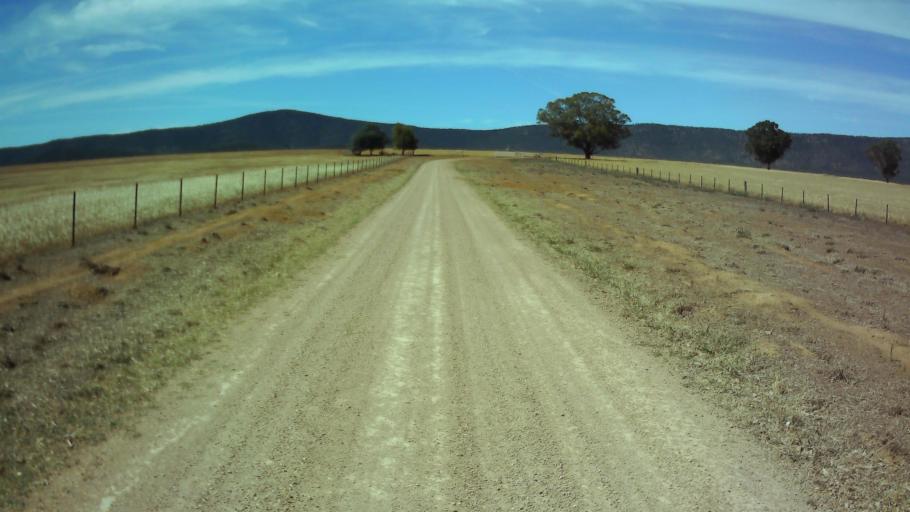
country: AU
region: New South Wales
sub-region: Weddin
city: Grenfell
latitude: -33.9487
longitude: 148.0664
